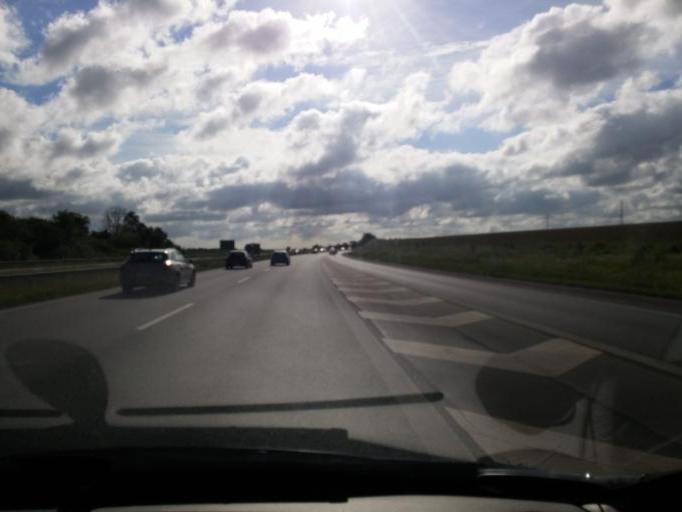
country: DK
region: Zealand
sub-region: Ringsted Kommune
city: Ringsted
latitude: 55.4558
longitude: 11.8318
